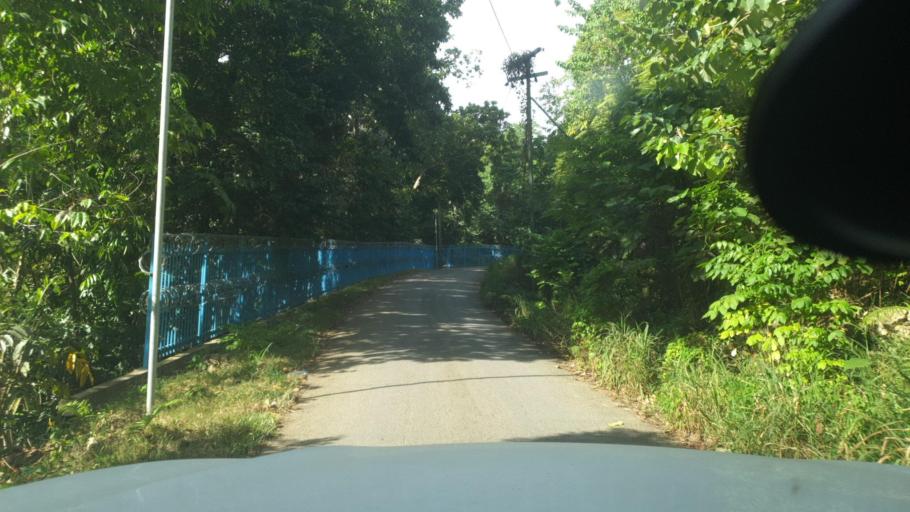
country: SB
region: Guadalcanal
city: Honiara
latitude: -9.4366
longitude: 159.9405
